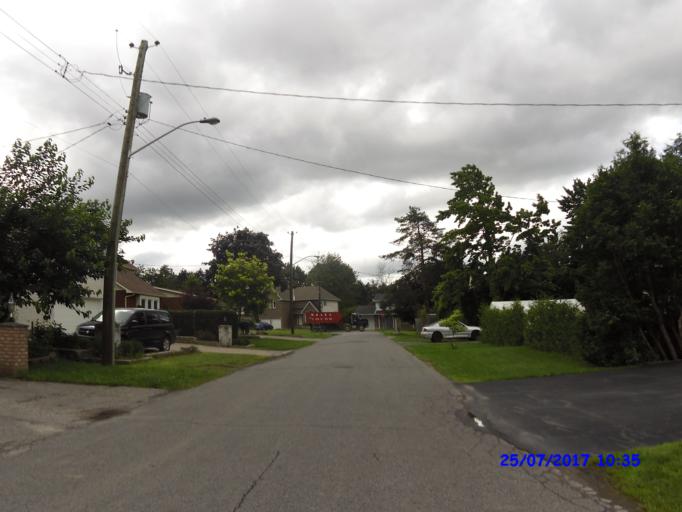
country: CA
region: Ontario
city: Ottawa
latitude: 45.3646
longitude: -75.7023
